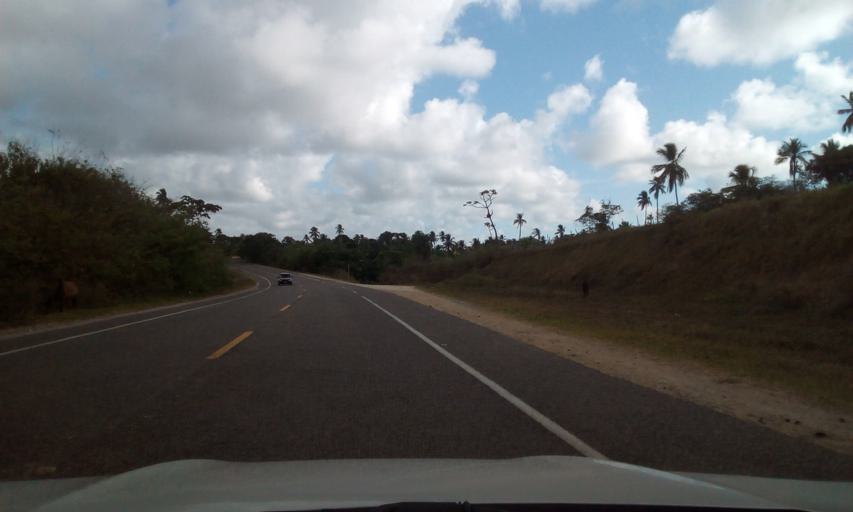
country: BR
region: Bahia
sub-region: Conde
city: Conde
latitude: -11.8006
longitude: -37.6279
